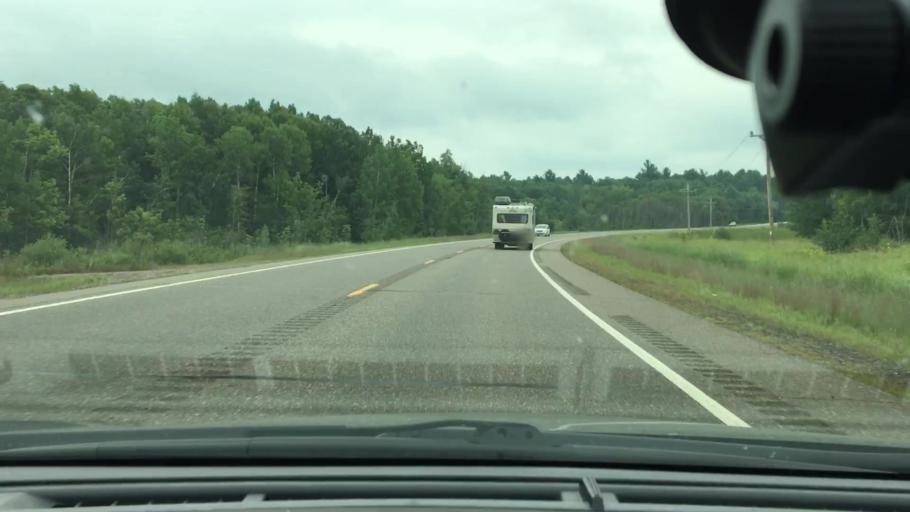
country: US
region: Minnesota
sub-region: Crow Wing County
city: Crosby
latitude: 46.5051
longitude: -93.9578
